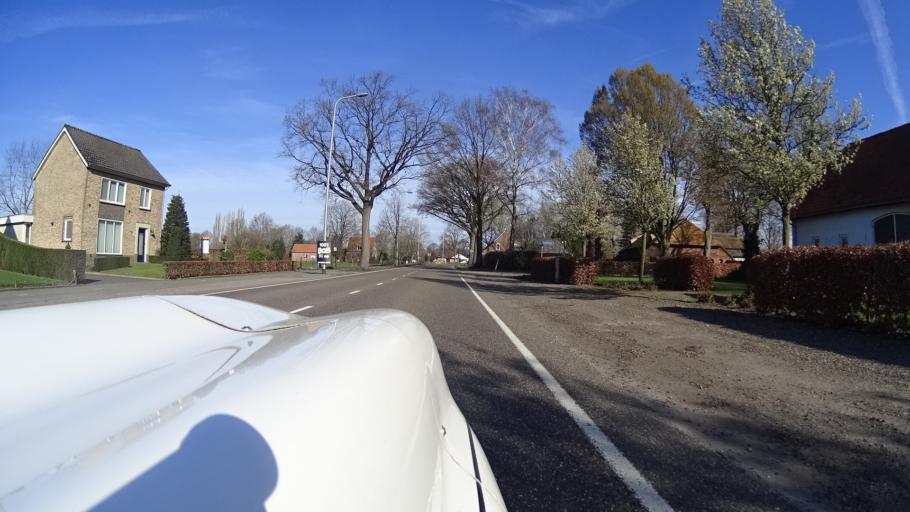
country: NL
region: North Brabant
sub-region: Gemeente Boekel
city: Boekel
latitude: 51.6149
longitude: 5.6693
